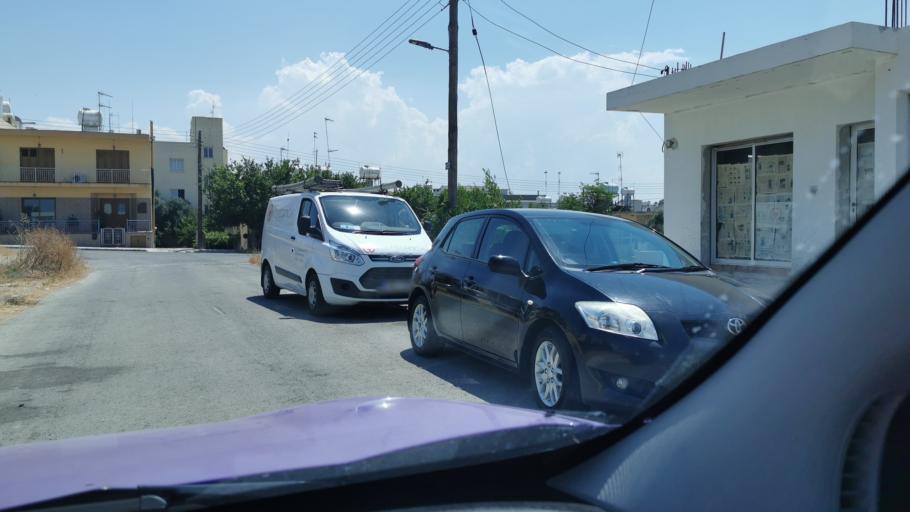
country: CY
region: Lefkosia
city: Kato Deftera
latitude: 35.1179
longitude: 33.2865
